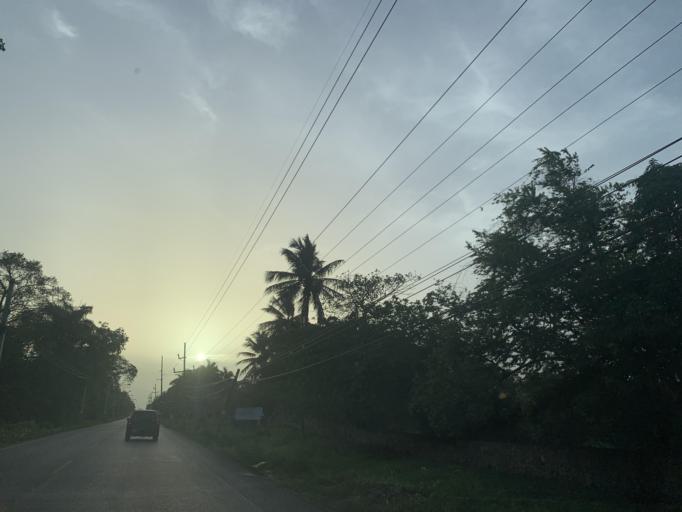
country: DO
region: Puerto Plata
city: Cabarete
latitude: 19.7765
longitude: -70.4696
